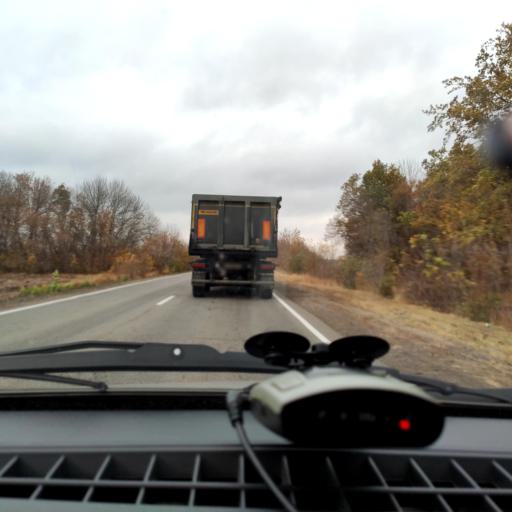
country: RU
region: Voronezj
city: Shilovo
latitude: 51.4410
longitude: 38.9968
